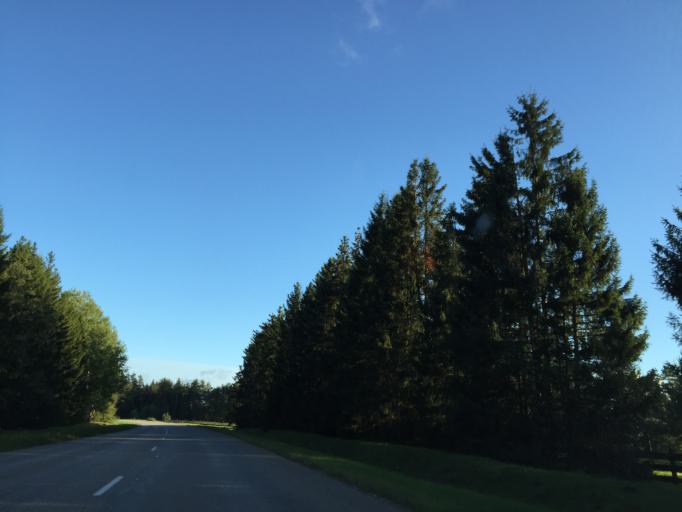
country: LV
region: Kuldigas Rajons
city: Kuldiga
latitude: 56.9157
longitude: 22.0550
